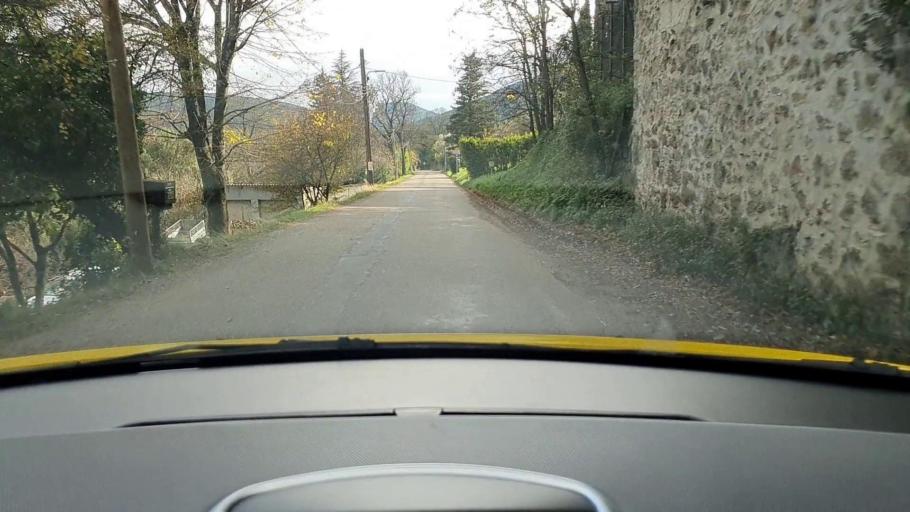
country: FR
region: Languedoc-Roussillon
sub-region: Departement du Gard
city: Branoux-les-Taillades
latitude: 44.2234
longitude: 3.9873
